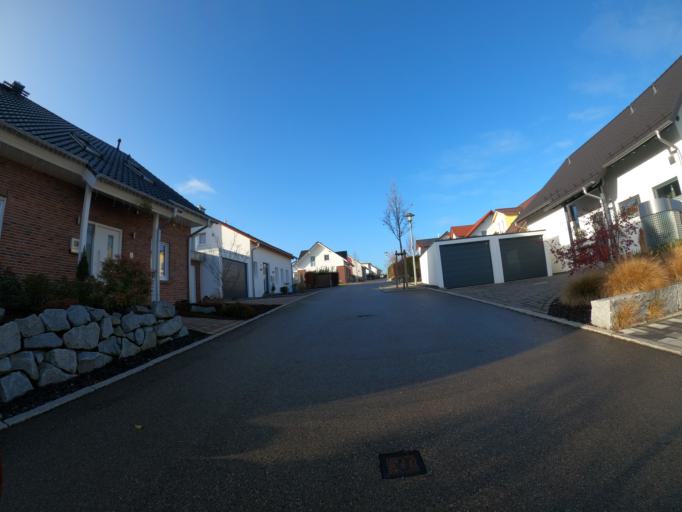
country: DE
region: Baden-Wuerttemberg
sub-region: Regierungsbezirk Stuttgart
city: Hattenhofen
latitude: 48.6689
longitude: 9.5687
